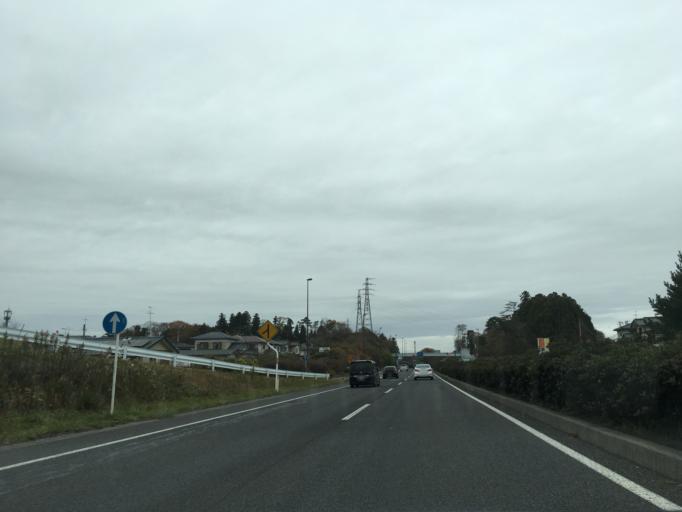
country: JP
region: Fukushima
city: Koriyama
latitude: 37.3486
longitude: 140.3564
